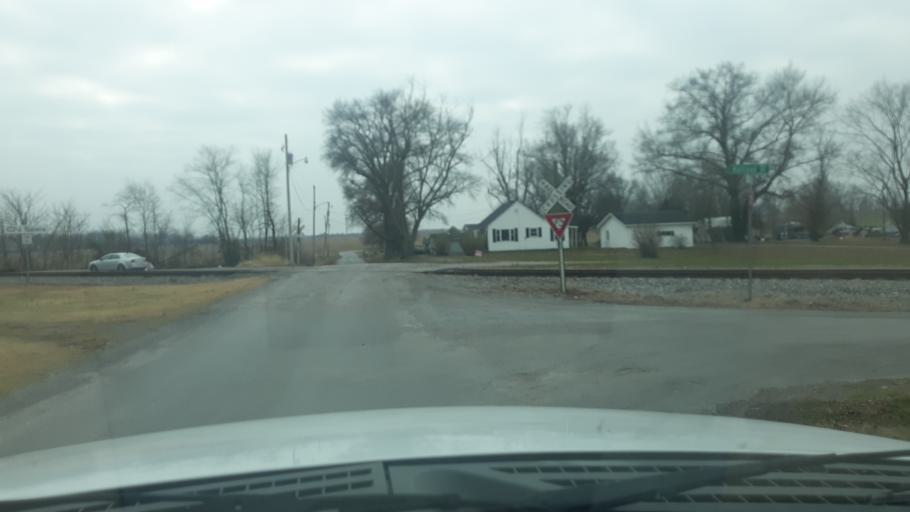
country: US
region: Illinois
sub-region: Saline County
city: Harrisburg
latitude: 37.8363
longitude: -88.6120
